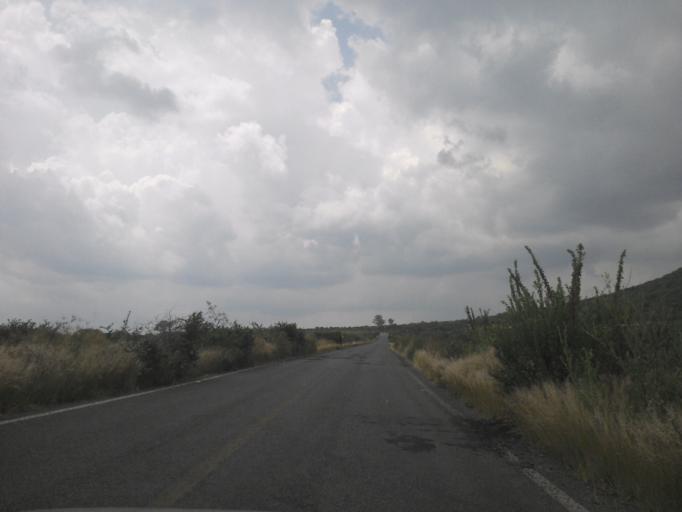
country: MX
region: Jalisco
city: San Diego de Alejandria
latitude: 20.9007
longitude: -101.9810
